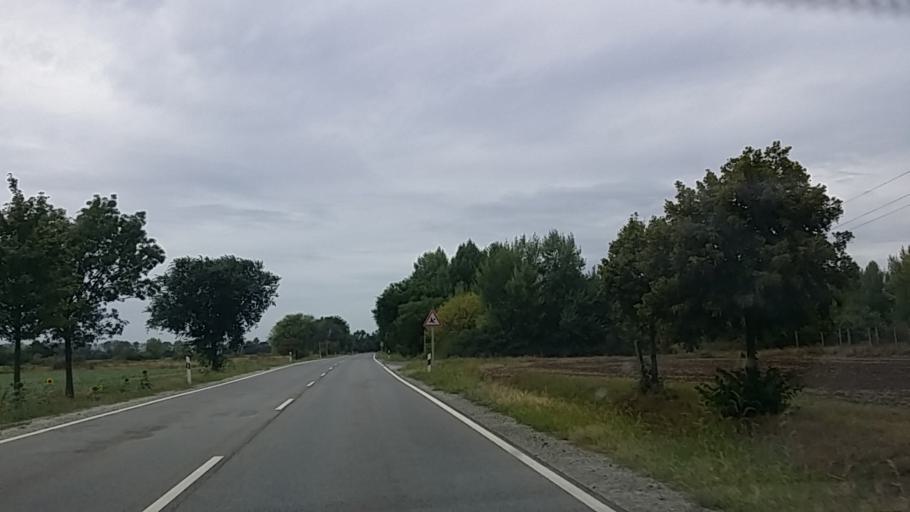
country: HU
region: Gyor-Moson-Sopron
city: Fertoszentmiklos
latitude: 47.5931
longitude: 16.8434
